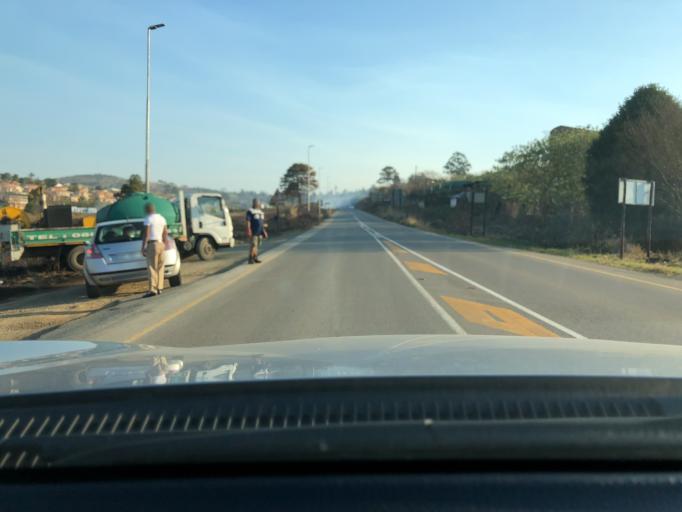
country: ZA
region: KwaZulu-Natal
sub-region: Sisonke District Municipality
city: Ixopo
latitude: -30.1457
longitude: 30.0703
